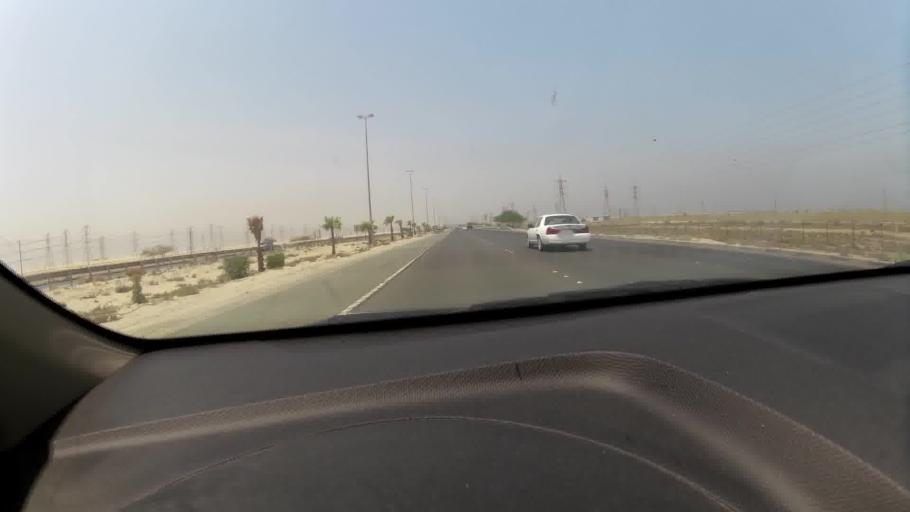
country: KW
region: Al Ahmadi
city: Al Fahahil
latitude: 28.8478
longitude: 48.2461
